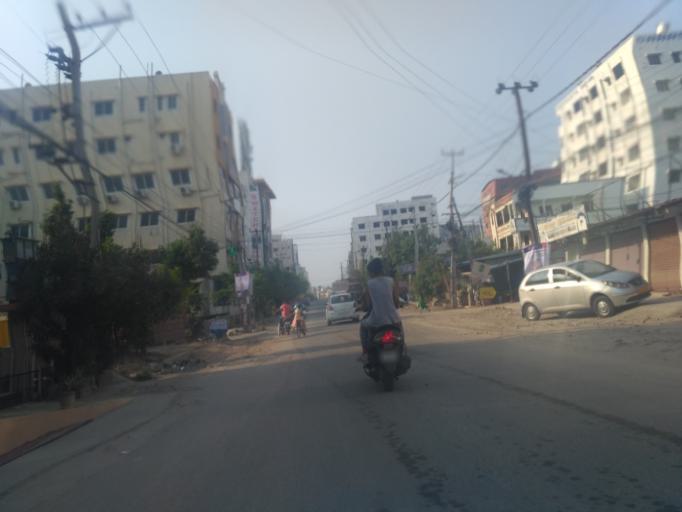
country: IN
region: Telangana
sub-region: Rangareddi
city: Kukatpalli
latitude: 17.4508
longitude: 78.3917
